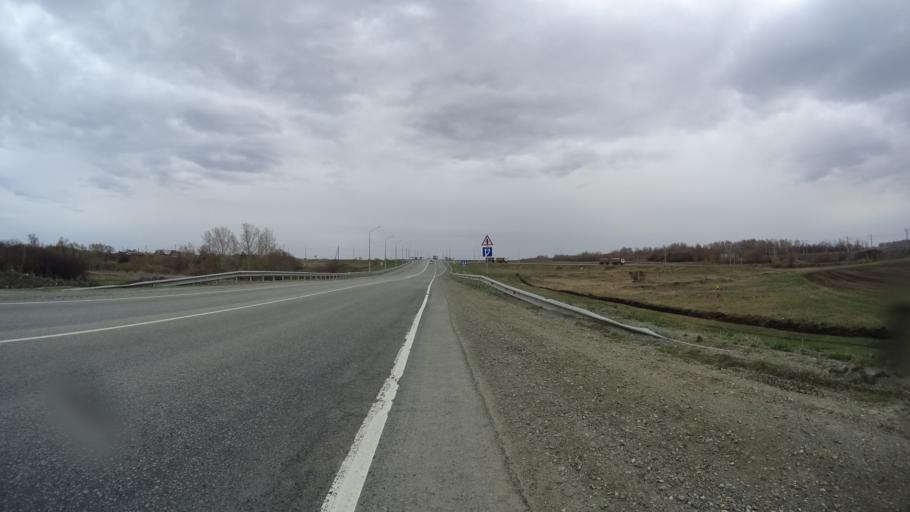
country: RU
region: Chelyabinsk
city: Krasnogorskiy
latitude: 54.6761
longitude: 61.2482
